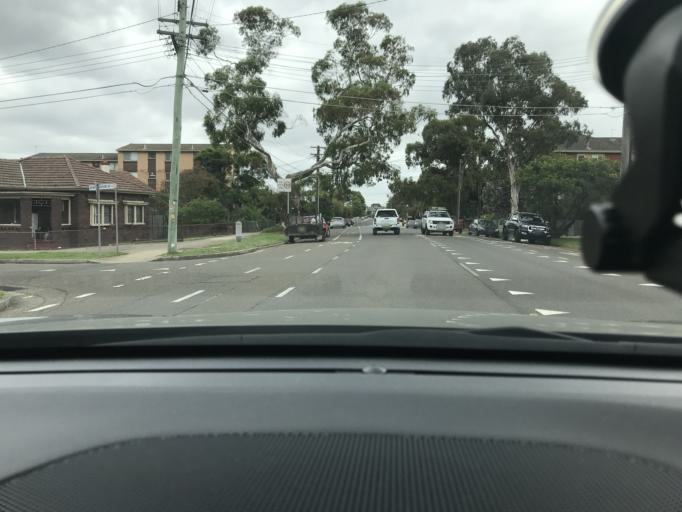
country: AU
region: New South Wales
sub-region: Canada Bay
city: Wareemba
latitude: -33.8526
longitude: 151.1295
